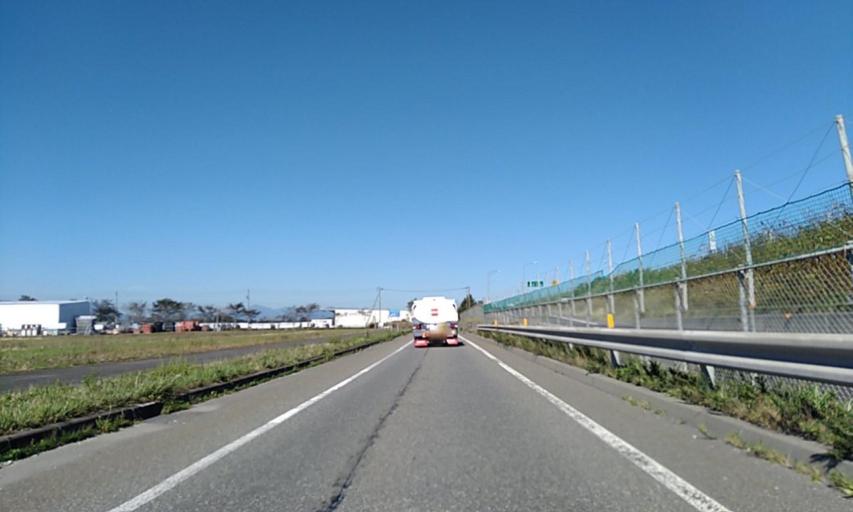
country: JP
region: Hokkaido
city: Tomakomai
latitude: 42.6881
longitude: 141.6974
